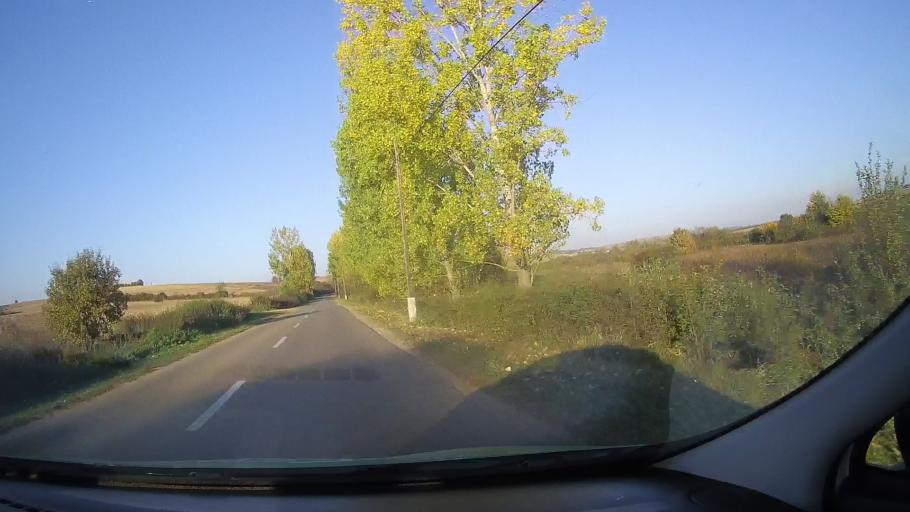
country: RO
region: Bihor
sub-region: Comuna Paleu
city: Paleu
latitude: 47.1237
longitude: 21.9630
